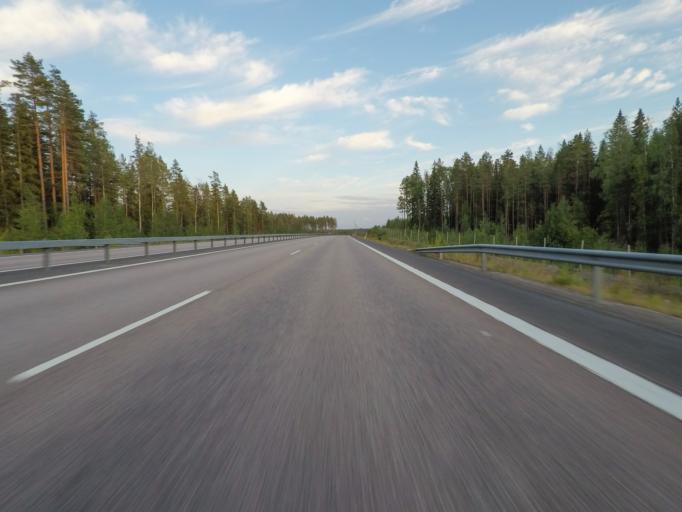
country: FI
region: Central Finland
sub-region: Jyvaeskylae
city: Toivakka
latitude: 62.1139
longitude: 25.9689
